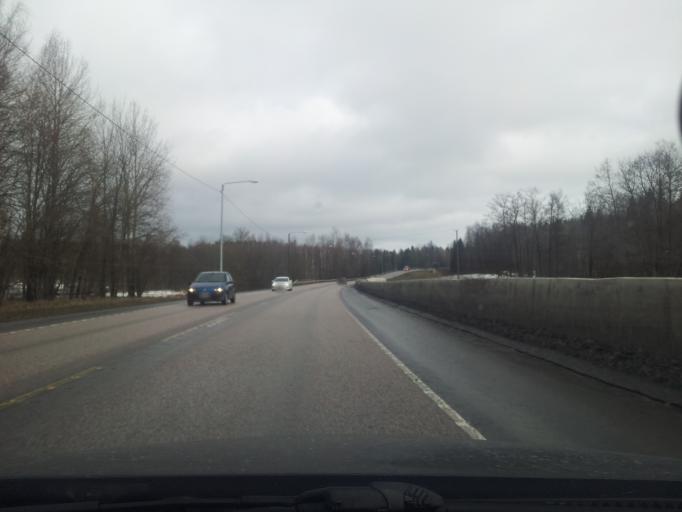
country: FI
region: Uusimaa
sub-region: Helsinki
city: Espoo
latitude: 60.1945
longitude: 24.5827
